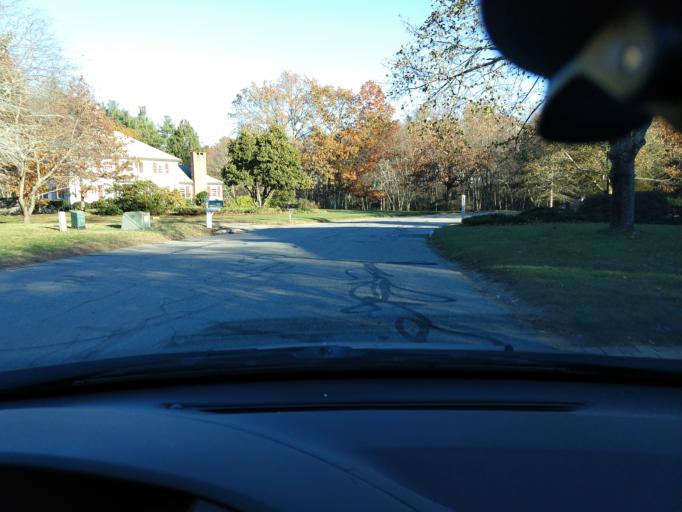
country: US
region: Massachusetts
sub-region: Middlesex County
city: Carlisle
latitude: 42.5004
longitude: -71.3232
